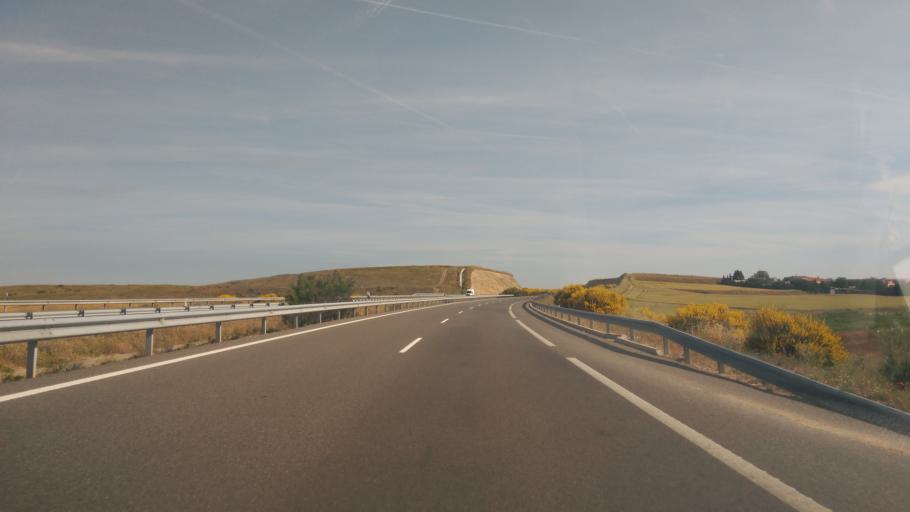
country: ES
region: Castille and Leon
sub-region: Provincia de Salamanca
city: Villamayor
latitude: 41.0066
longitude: -5.6793
